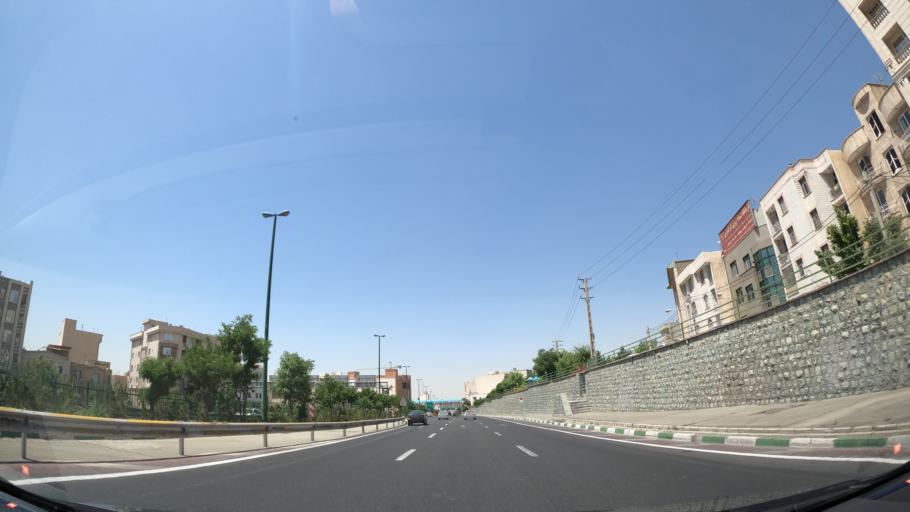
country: IR
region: Tehran
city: Tajrish
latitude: 35.7672
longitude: 51.3098
